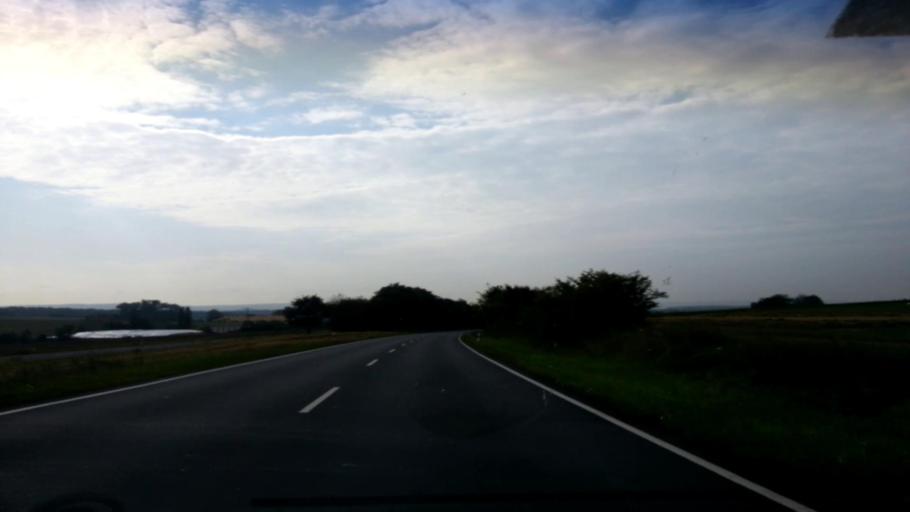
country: DE
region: Bavaria
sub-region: Regierungsbezirk Unterfranken
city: Lulsfeld
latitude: 49.8530
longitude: 10.3522
